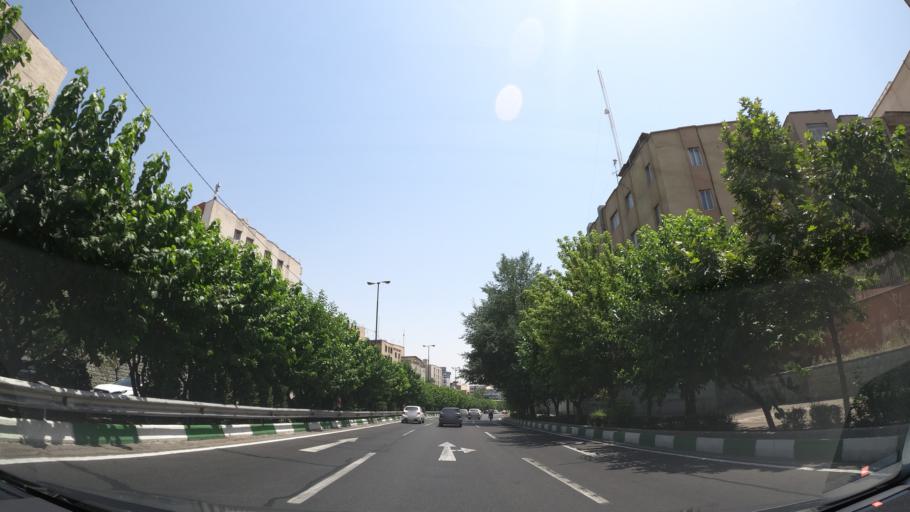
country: IR
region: Tehran
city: Tehran
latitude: 35.7264
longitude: 51.4240
